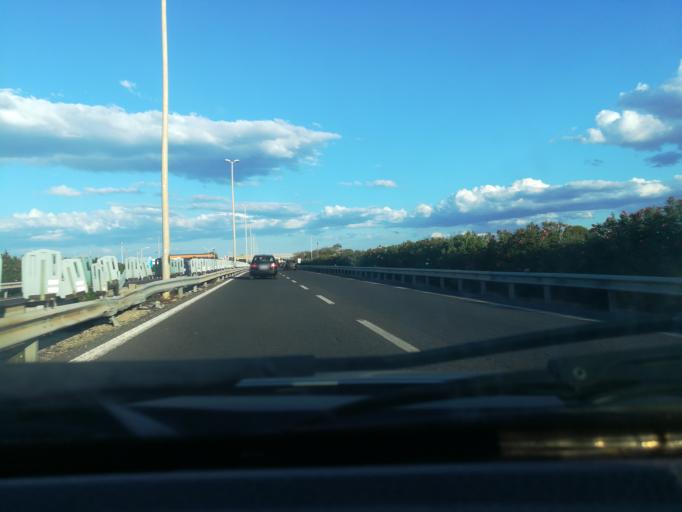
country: IT
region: Apulia
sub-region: Provincia di Bari
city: Mola di Bari
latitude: 41.0783
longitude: 17.0430
